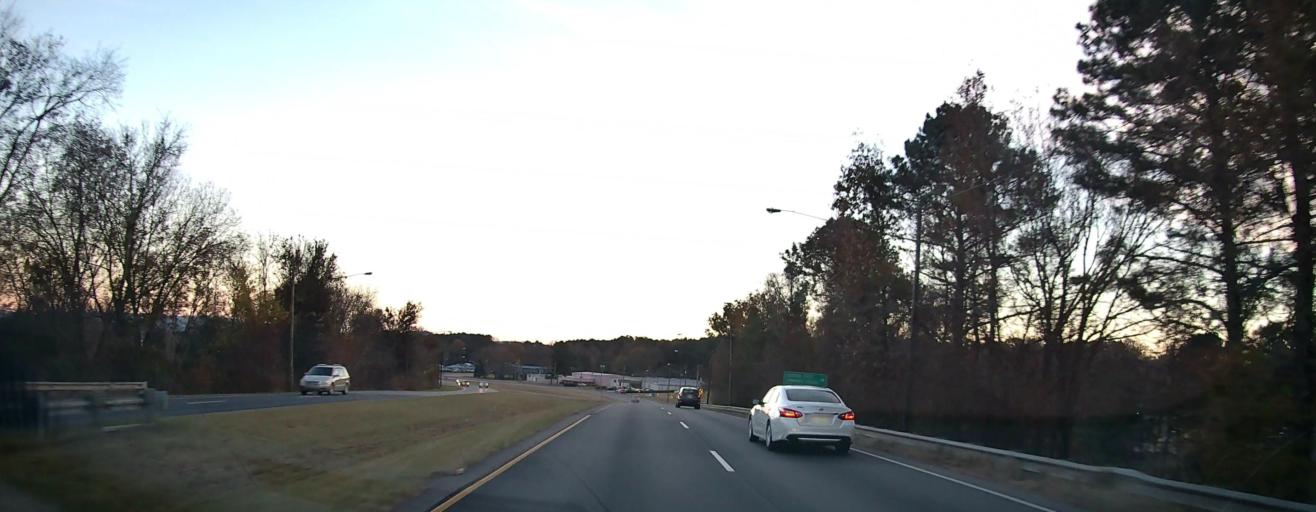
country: US
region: Alabama
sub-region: Etowah County
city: Glencoe
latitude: 33.9888
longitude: -85.9667
